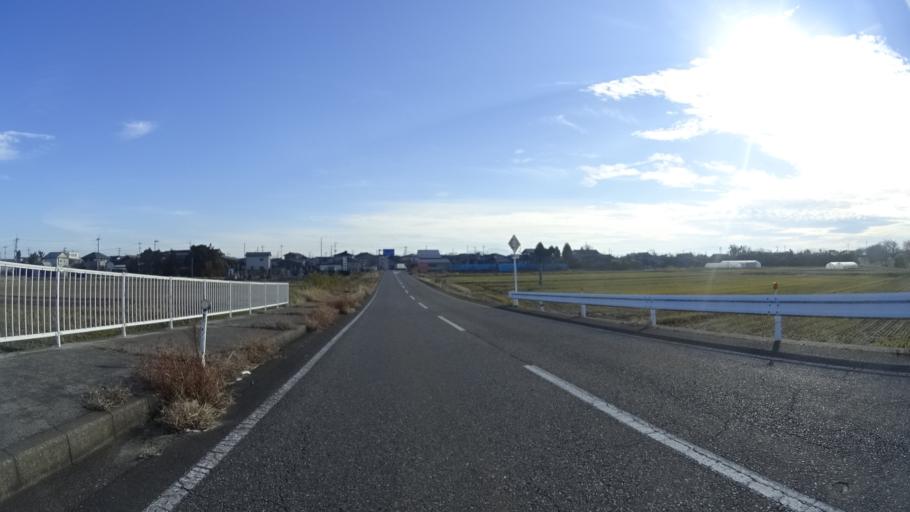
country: JP
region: Niigata
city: Yoshida-kasugacho
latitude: 37.6293
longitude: 138.8336
